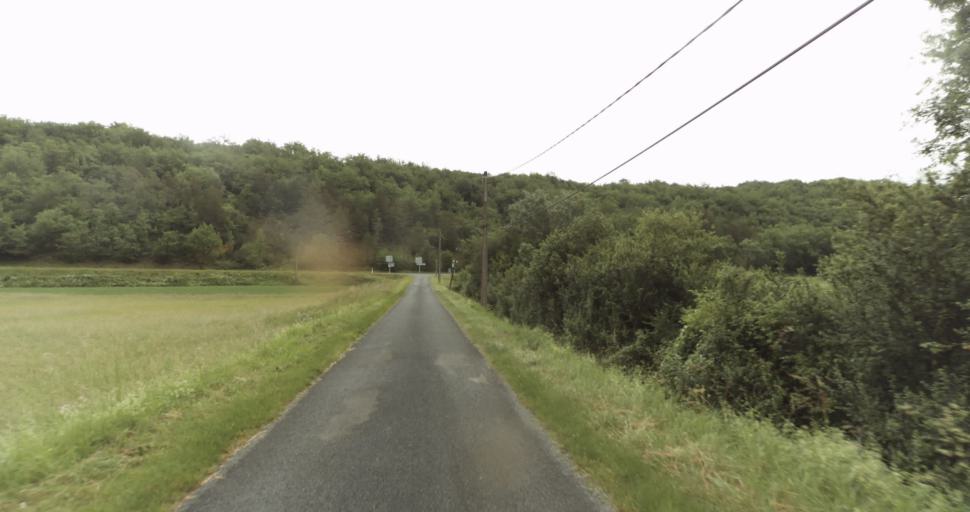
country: FR
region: Aquitaine
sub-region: Departement de la Dordogne
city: Beaumont-du-Perigord
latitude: 44.7510
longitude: 0.8393
